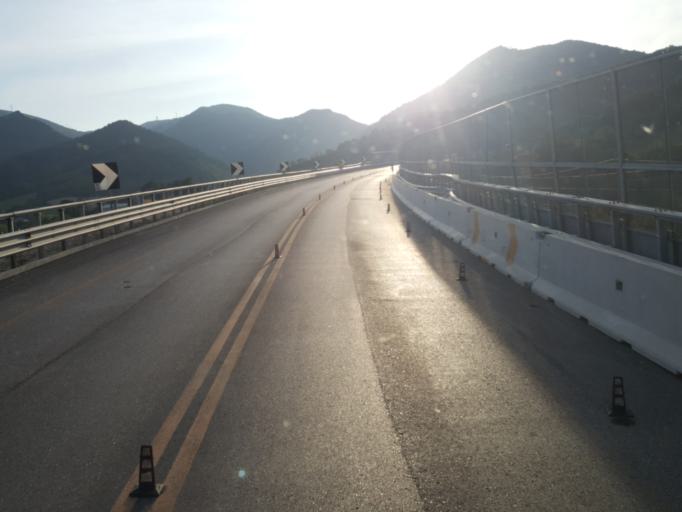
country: IT
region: Umbria
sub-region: Provincia di Perugia
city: Fossato di Vico
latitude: 43.3032
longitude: 12.8385
